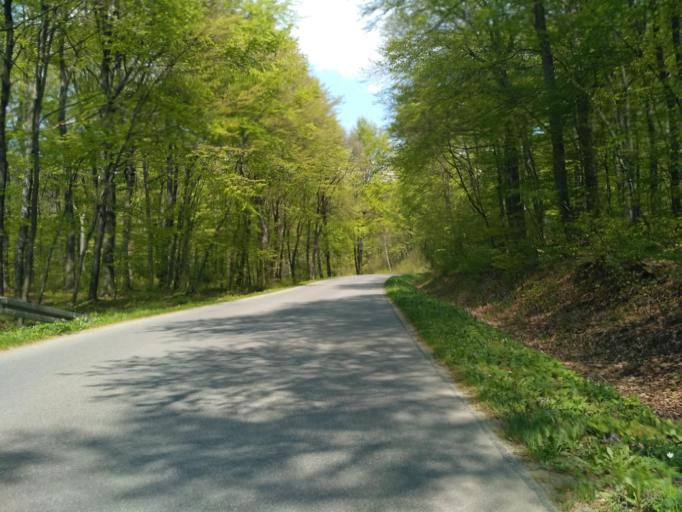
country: PL
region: Subcarpathian Voivodeship
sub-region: Powiat jasielski
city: Debowiec
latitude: 49.7029
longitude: 21.5111
